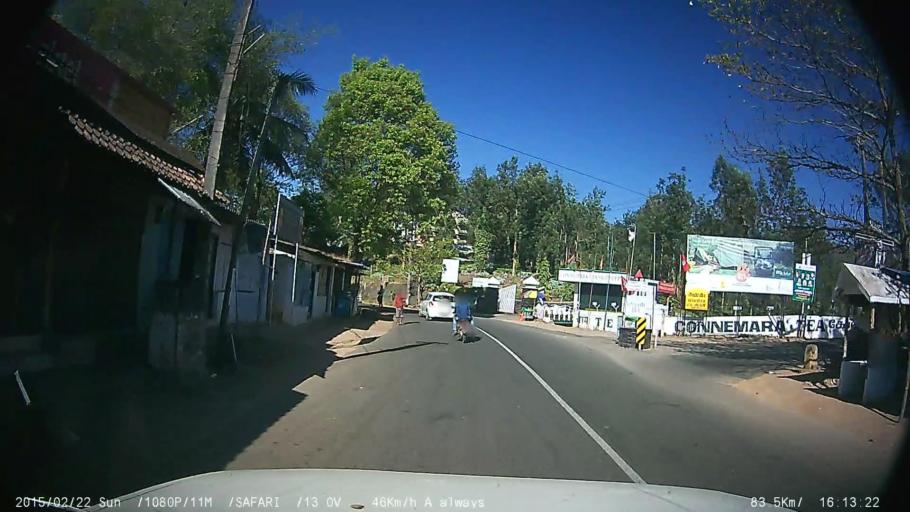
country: IN
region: Tamil Nadu
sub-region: Theni
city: Gudalur
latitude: 9.5778
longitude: 77.0968
